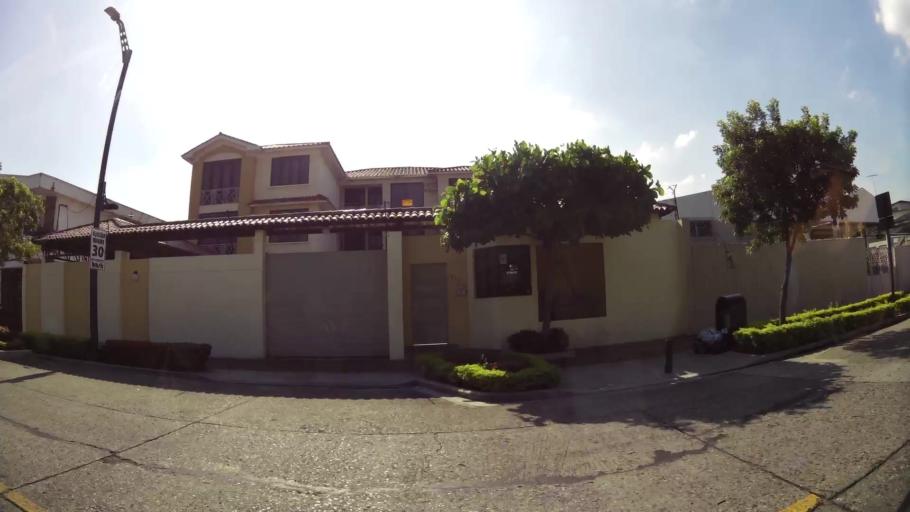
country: EC
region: Guayas
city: Guayaquil
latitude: -2.1646
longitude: -79.9359
